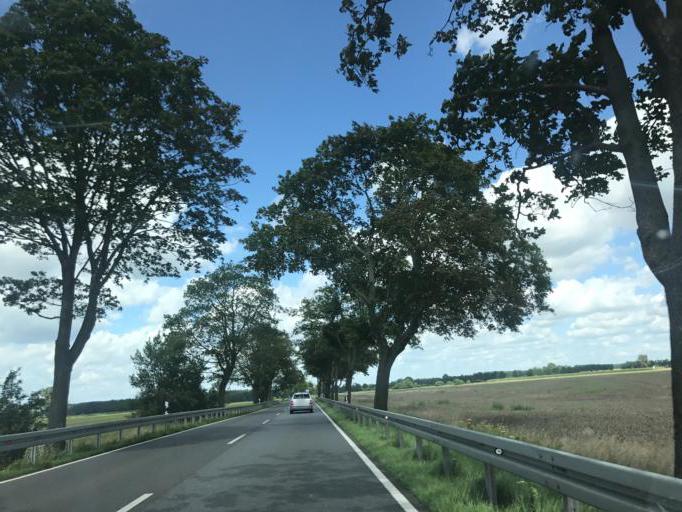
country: DE
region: Brandenburg
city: Oranienburg
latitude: 52.8309
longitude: 13.2034
